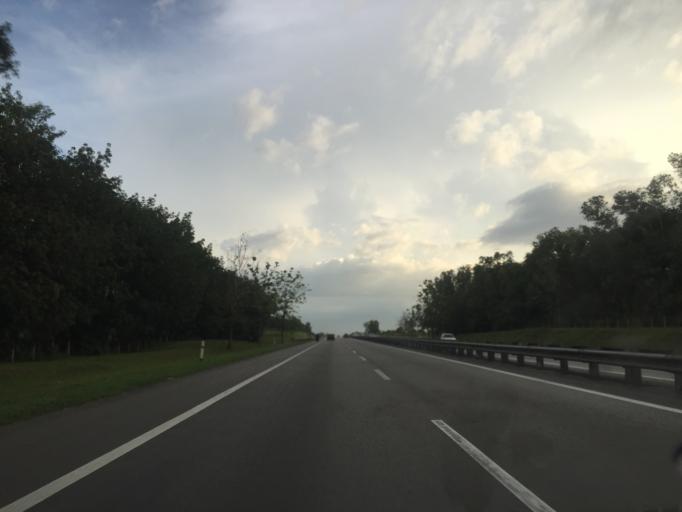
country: MY
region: Kedah
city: Bedong
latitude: 5.7234
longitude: 100.5231
